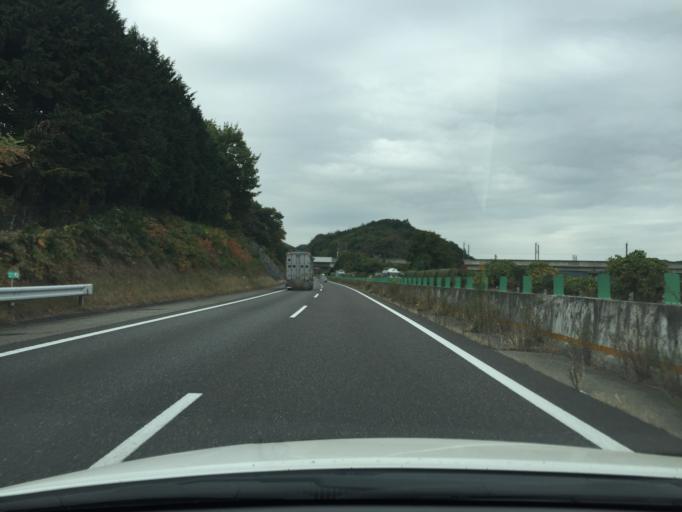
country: JP
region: Fukushima
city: Sukagawa
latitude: 37.1481
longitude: 140.2166
